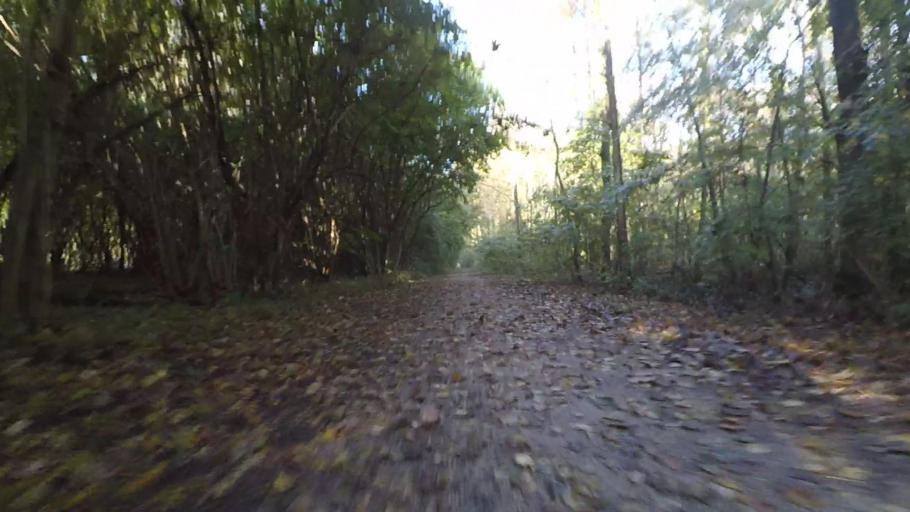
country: NL
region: Flevoland
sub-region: Gemeente Zeewolde
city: Zeewolde
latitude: 52.3008
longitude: 5.5323
